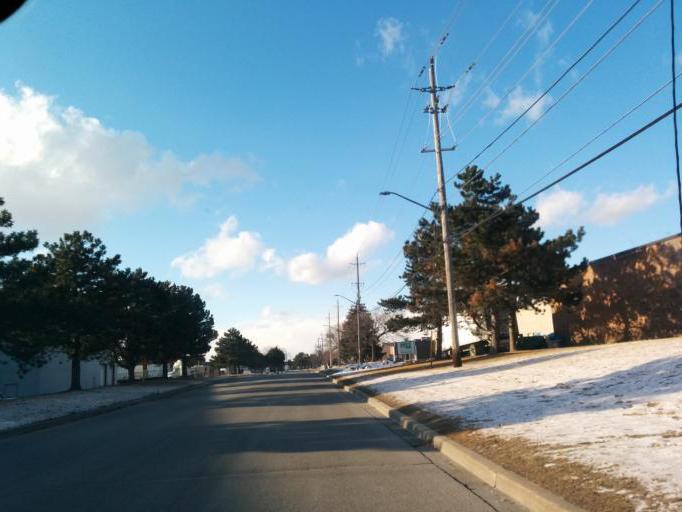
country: CA
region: Ontario
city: Etobicoke
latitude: 43.6366
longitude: -79.6270
